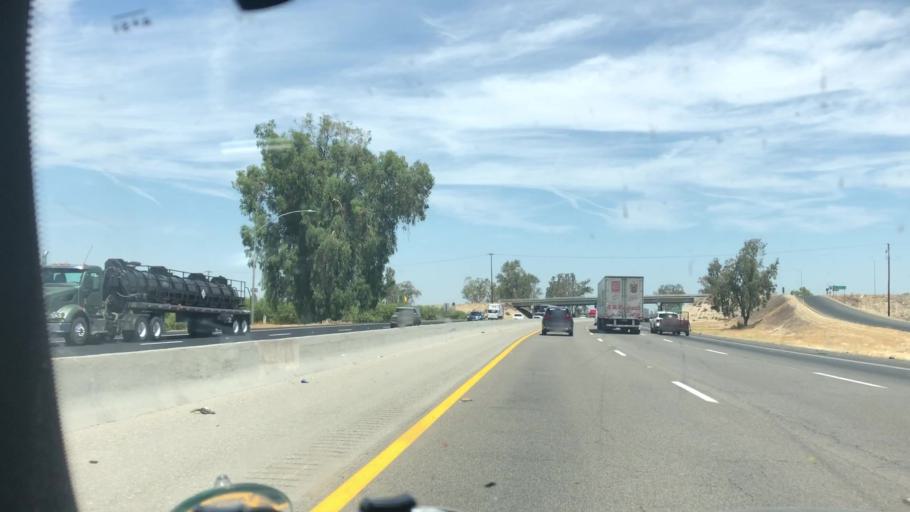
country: US
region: California
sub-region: Kern County
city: McFarland
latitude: 35.7157
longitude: -119.2364
